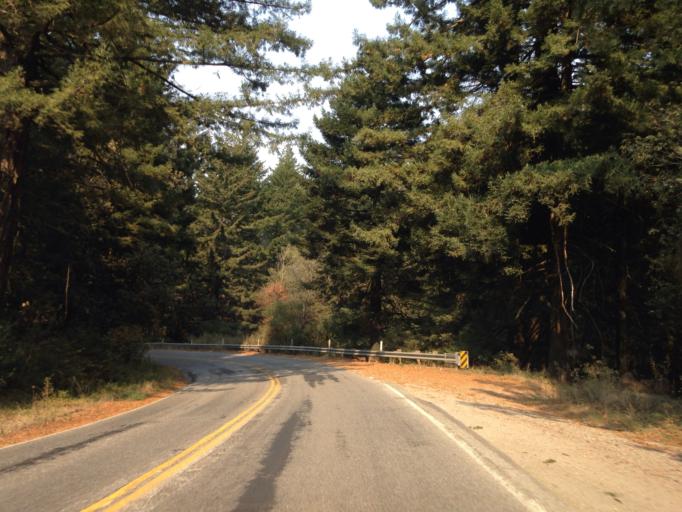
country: US
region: California
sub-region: San Mateo County
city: Highlands-Baywood Park
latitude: 37.4570
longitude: -122.3387
